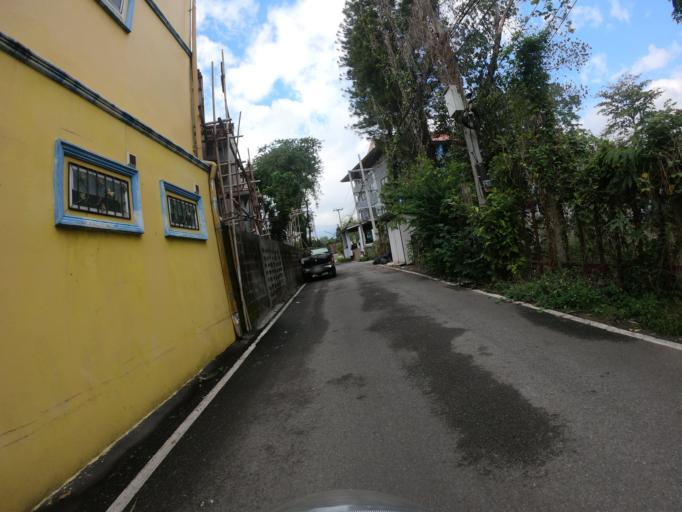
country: TH
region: Chiang Mai
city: Chiang Mai
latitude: 18.8119
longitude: 98.9800
